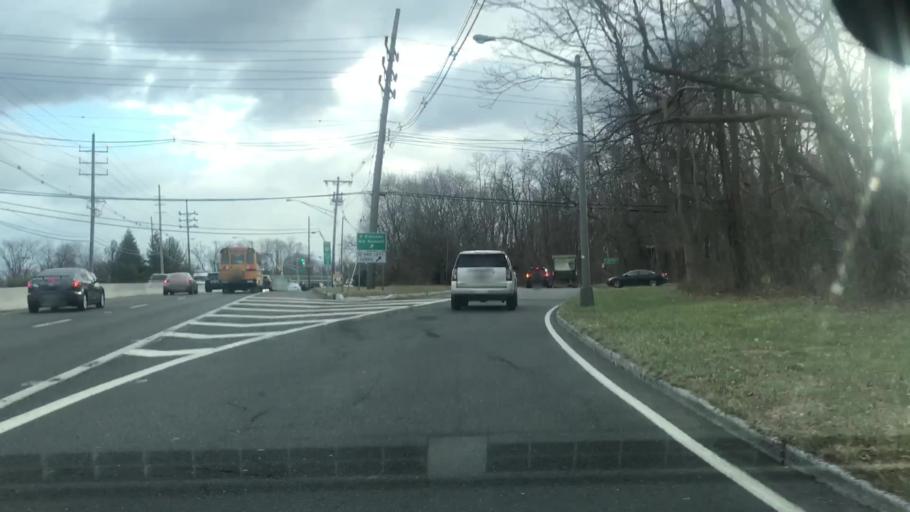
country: US
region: New Jersey
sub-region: Monmouth County
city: Keansburg
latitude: 40.4109
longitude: -74.1364
